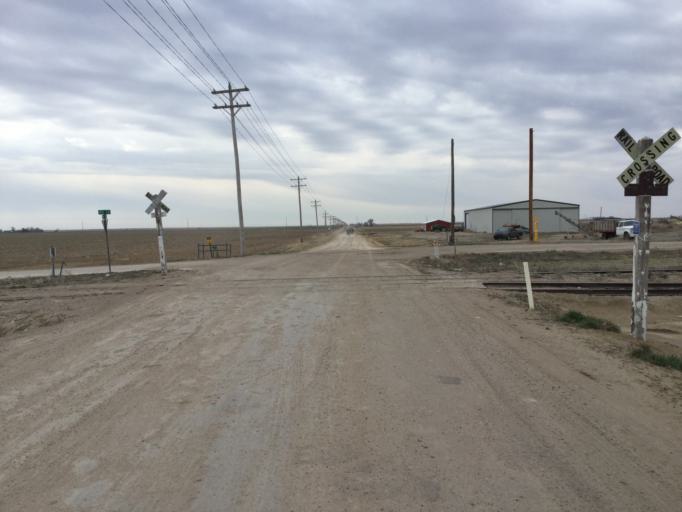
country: US
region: Kansas
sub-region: Stanton County
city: Johnson
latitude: 37.5627
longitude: -101.7435
